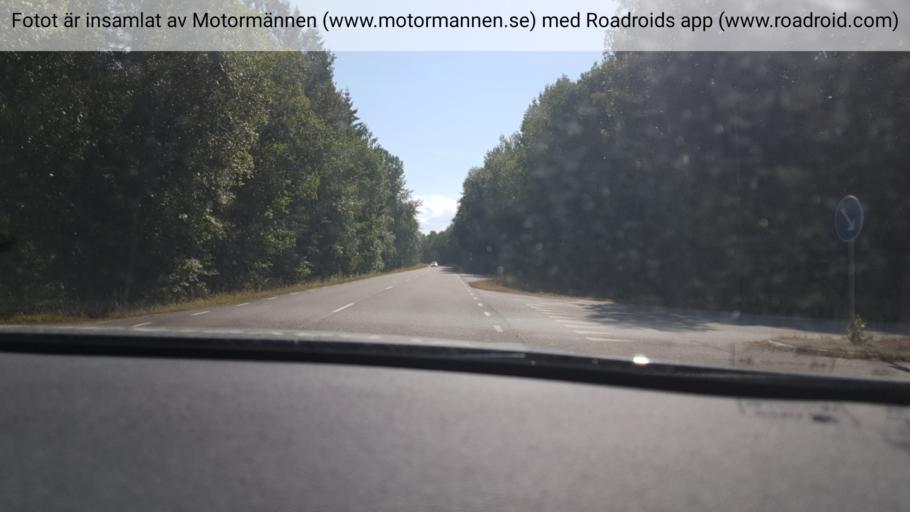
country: SE
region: Vaestra Goetaland
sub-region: Gotene Kommun
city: Kallby
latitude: 58.5980
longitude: 13.3893
